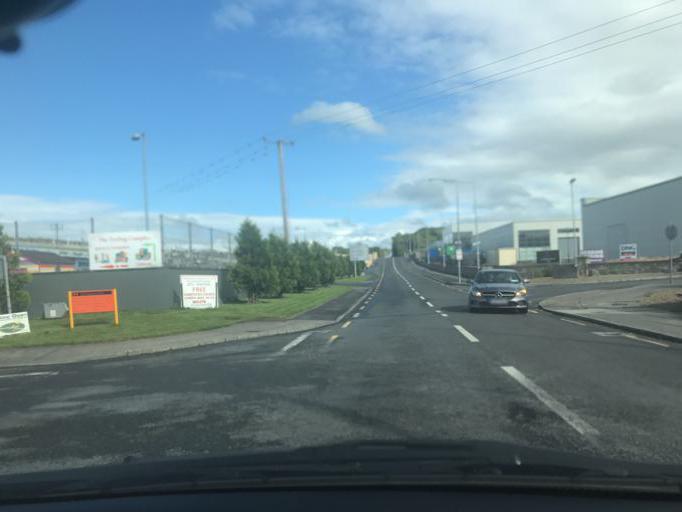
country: IE
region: Connaught
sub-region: Sligo
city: Collooney
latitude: 54.1828
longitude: -8.4839
